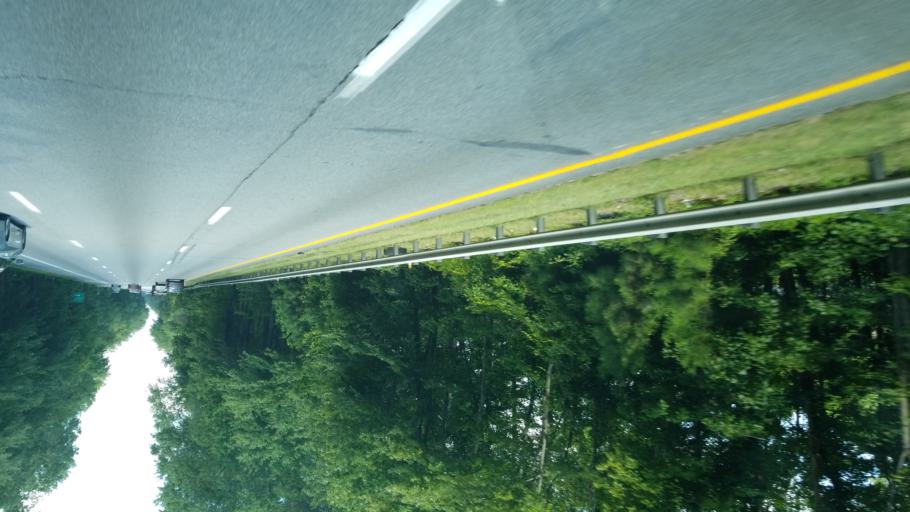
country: US
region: Virginia
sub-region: City of Suffolk
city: Suffolk
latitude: 36.7552
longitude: -76.5116
